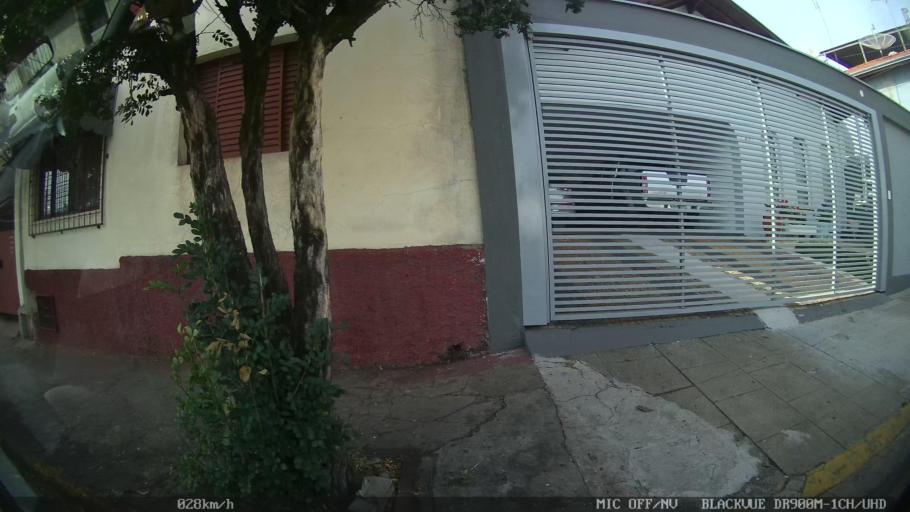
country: BR
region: Sao Paulo
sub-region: Piracicaba
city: Piracicaba
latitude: -22.7431
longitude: -47.6505
